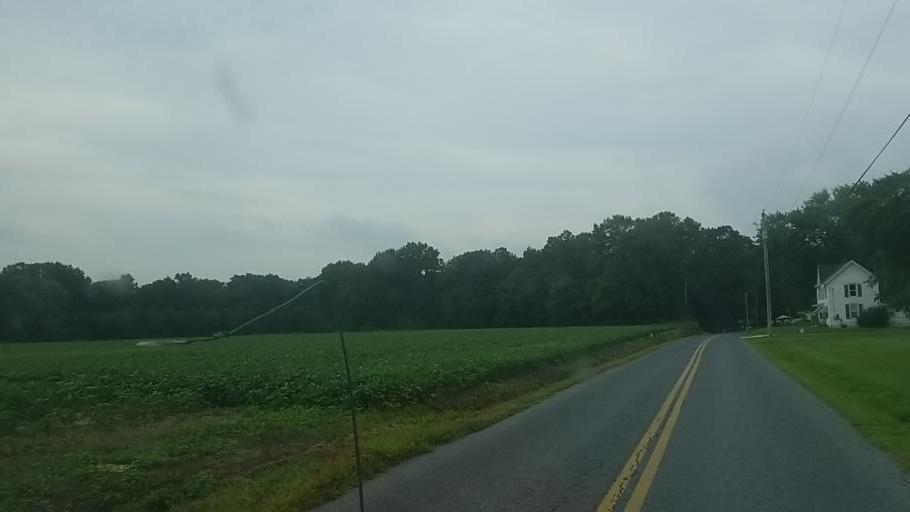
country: US
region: Delaware
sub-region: Sussex County
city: Selbyville
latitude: 38.4369
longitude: -75.1948
